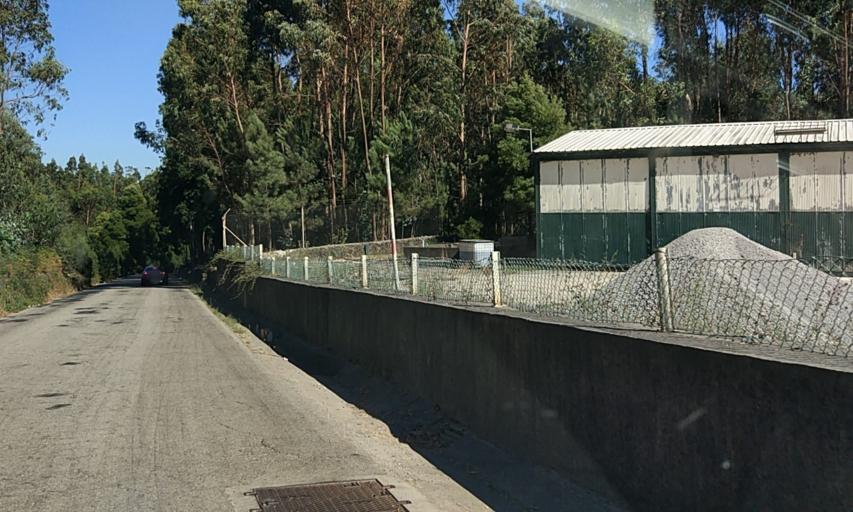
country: PT
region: Porto
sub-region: Maia
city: Anta
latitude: 41.2950
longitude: -8.6187
